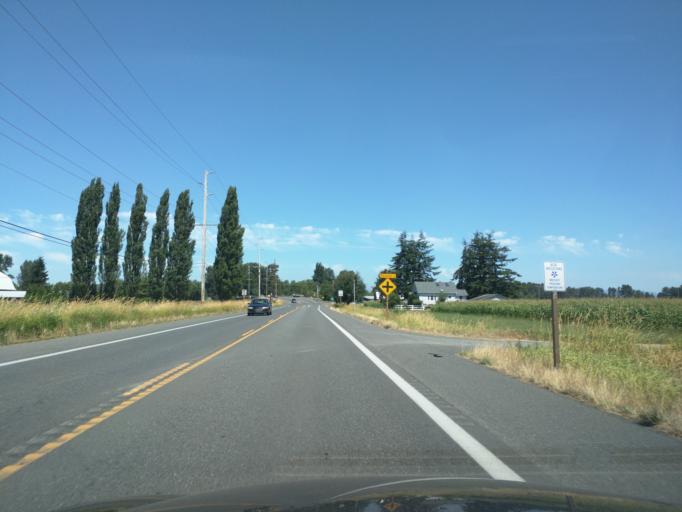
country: US
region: Washington
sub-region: Whatcom County
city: Lynden
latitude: 48.9330
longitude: -122.4416
